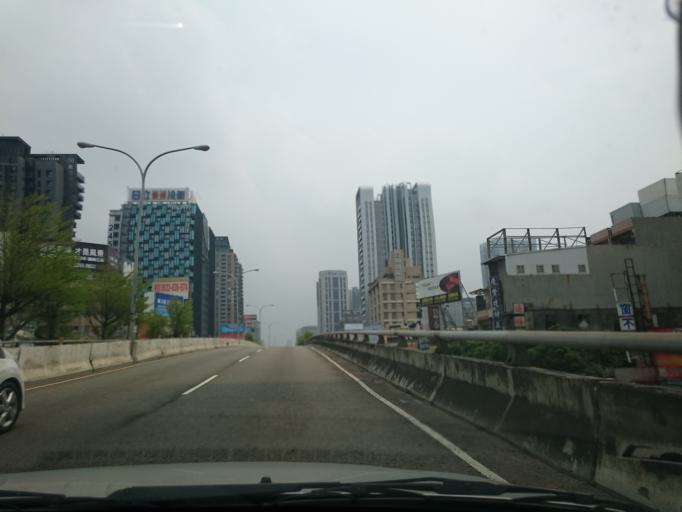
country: TW
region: Taiwan
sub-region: Taichung City
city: Taichung
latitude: 24.1715
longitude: 120.6359
